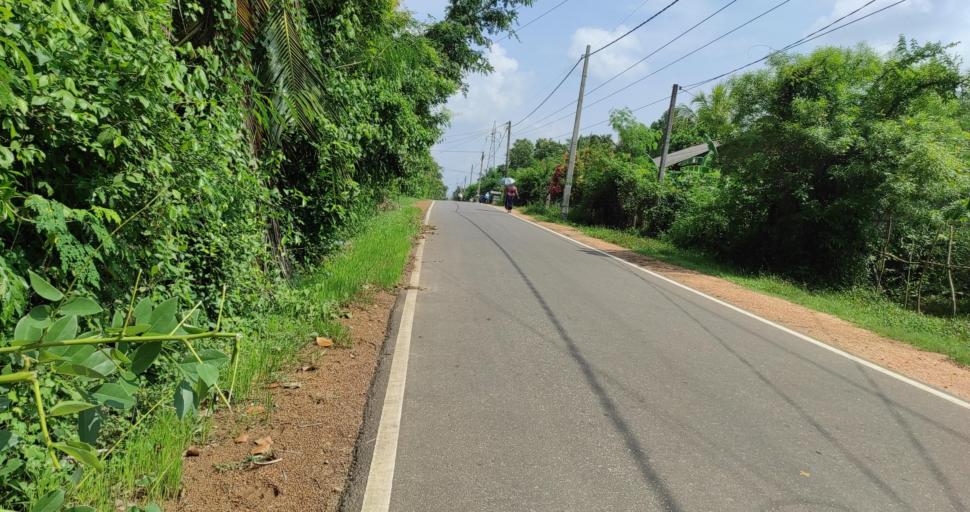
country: LK
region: Eastern Province
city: Trincomalee
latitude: 8.3783
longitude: 81.0150
